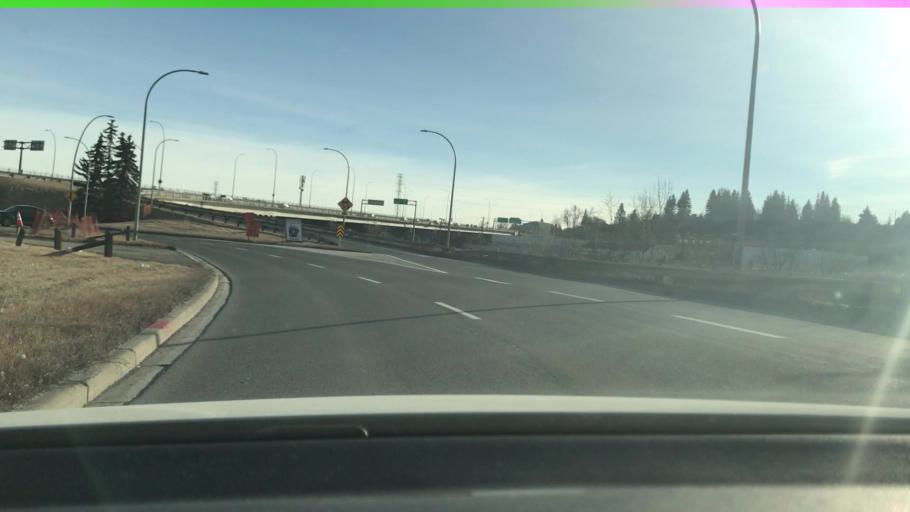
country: CA
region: Alberta
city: Calgary
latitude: 51.0487
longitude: -114.1177
